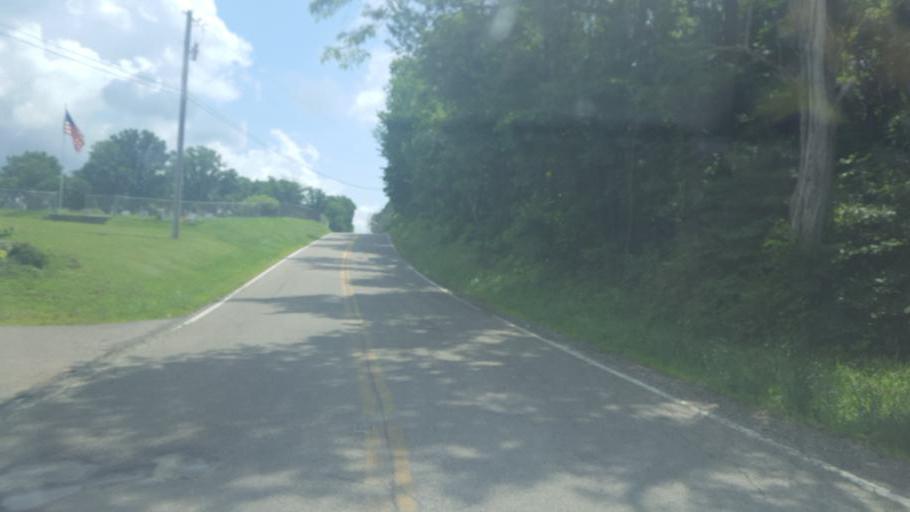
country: US
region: Ohio
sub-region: Ross County
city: Kingston
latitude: 39.4127
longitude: -82.7468
